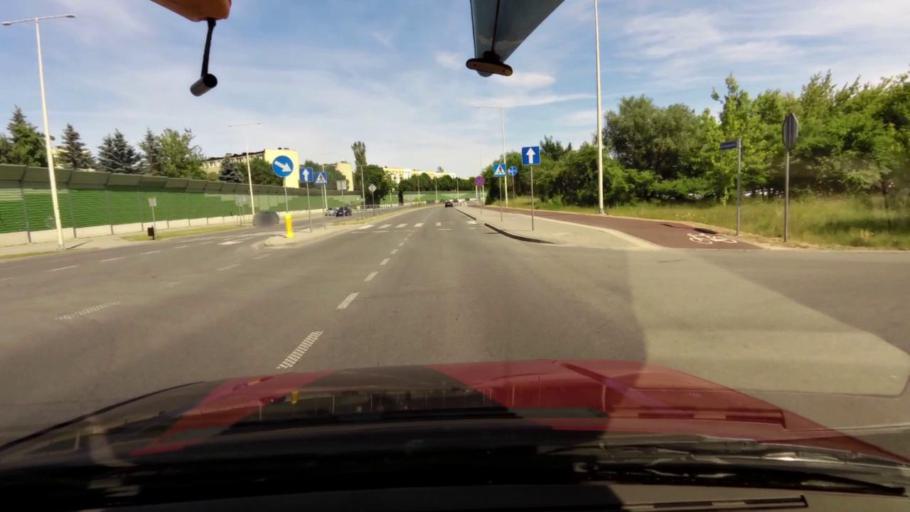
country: PL
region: Pomeranian Voivodeship
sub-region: Powiat slupski
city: Kobylnica
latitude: 54.4566
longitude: 16.9966
